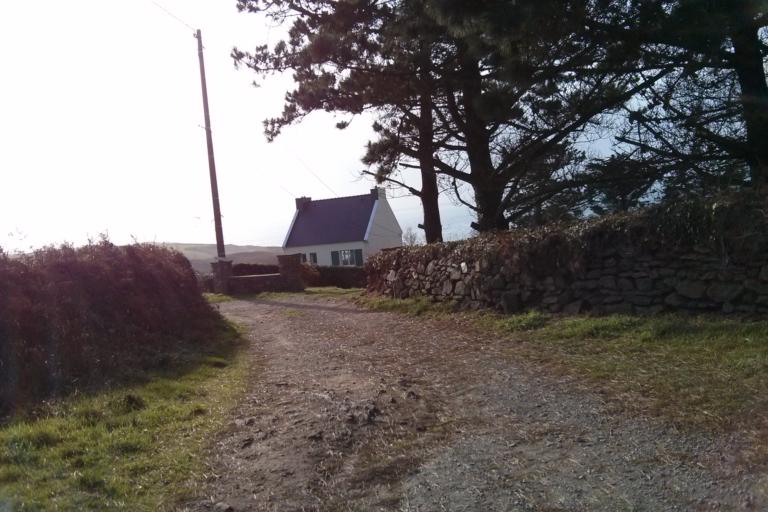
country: FR
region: Brittany
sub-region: Departement du Finistere
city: Le Conquet
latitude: 48.4006
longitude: -4.7705
